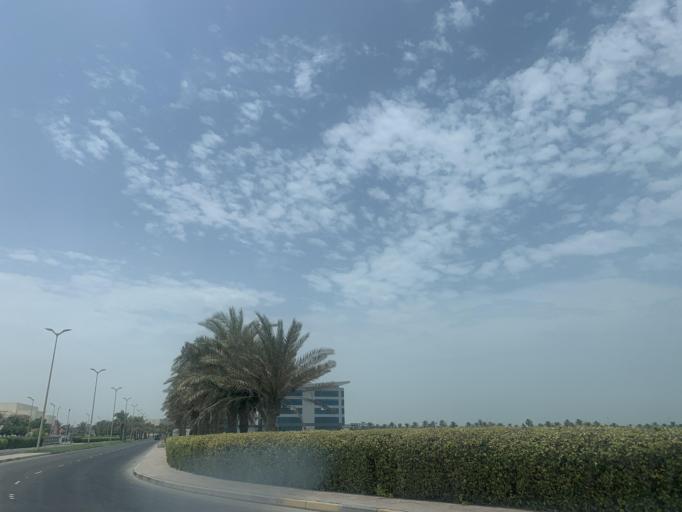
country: BH
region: Muharraq
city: Al Hadd
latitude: 26.2782
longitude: 50.6679
